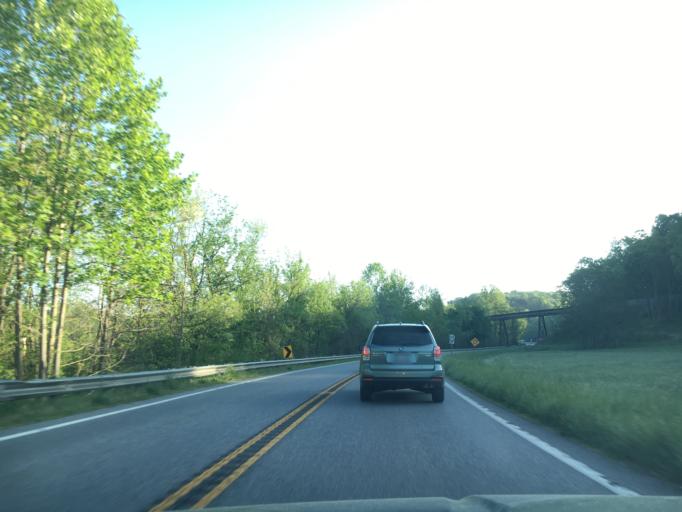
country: US
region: Virginia
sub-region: Campbell County
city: Rustburg
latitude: 37.3008
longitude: -79.1110
